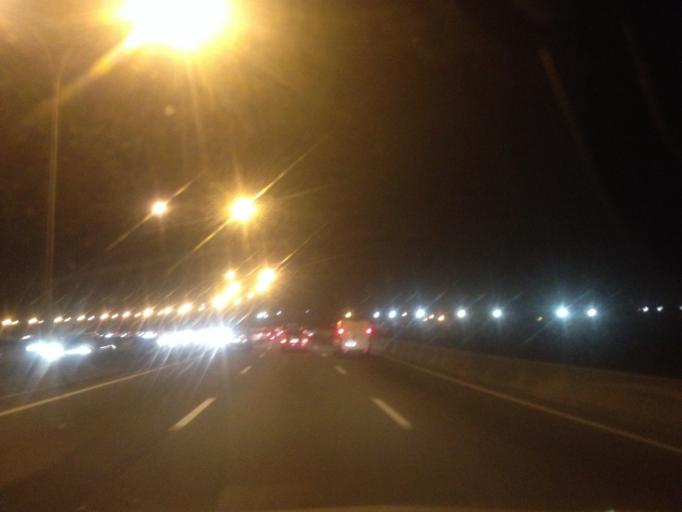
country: BR
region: Rio de Janeiro
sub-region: Duque De Caxias
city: Duque de Caxias
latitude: -22.8253
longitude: -43.2512
